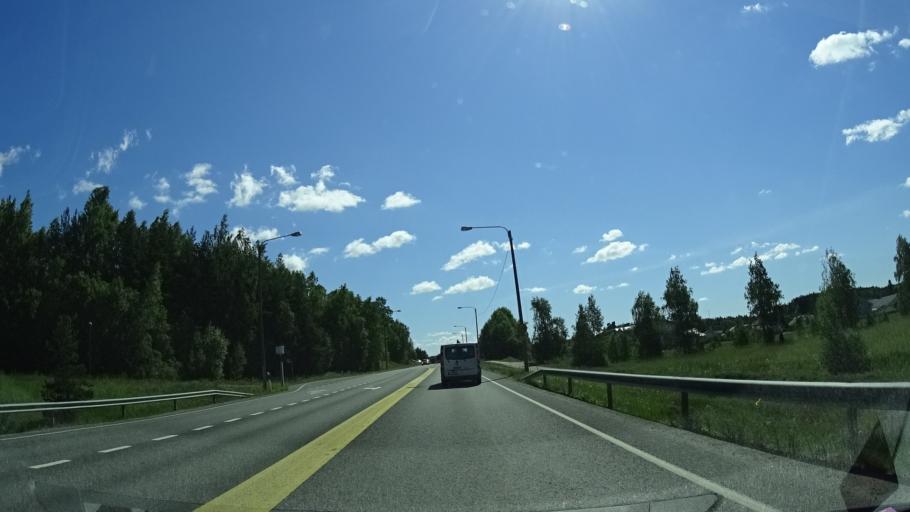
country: FI
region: Varsinais-Suomi
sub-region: Turku
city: Raisio
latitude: 60.5062
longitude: 22.1357
